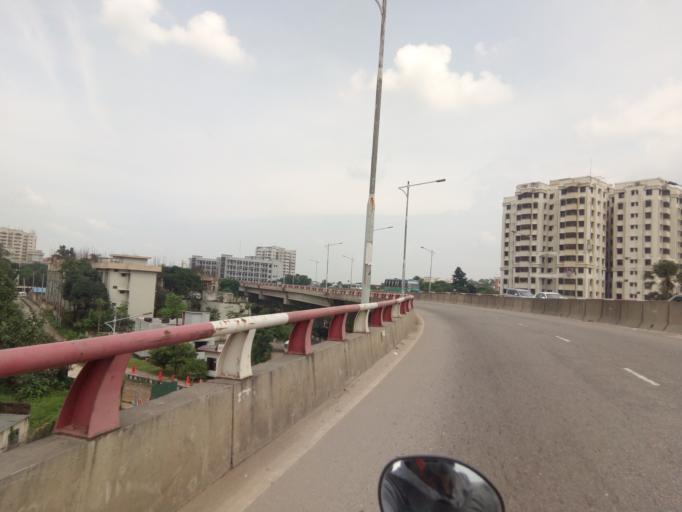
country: BD
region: Dhaka
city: Tungi
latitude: 23.8174
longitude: 90.3980
